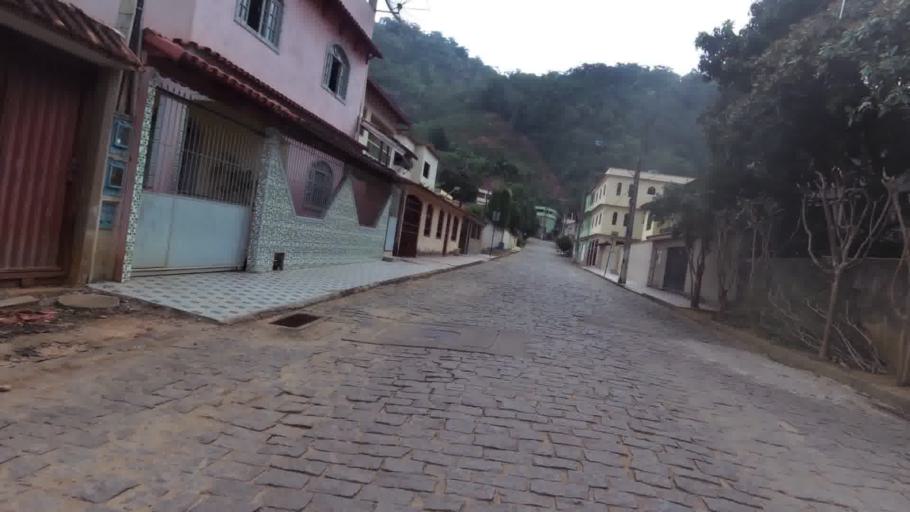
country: BR
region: Espirito Santo
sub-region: Alfredo Chaves
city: Alfredo Chaves
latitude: -20.6363
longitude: -40.7534
